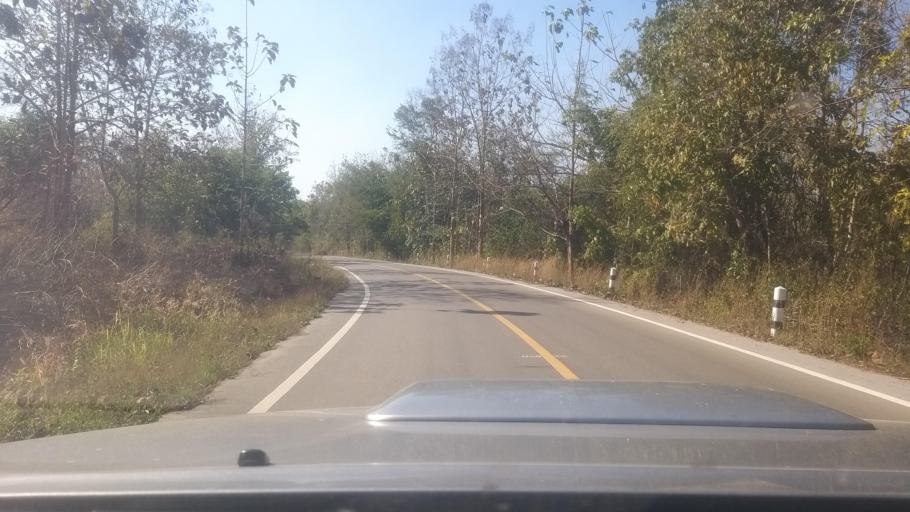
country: TH
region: Phrae
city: Nong Muang Khai
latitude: 18.2967
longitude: 100.0499
